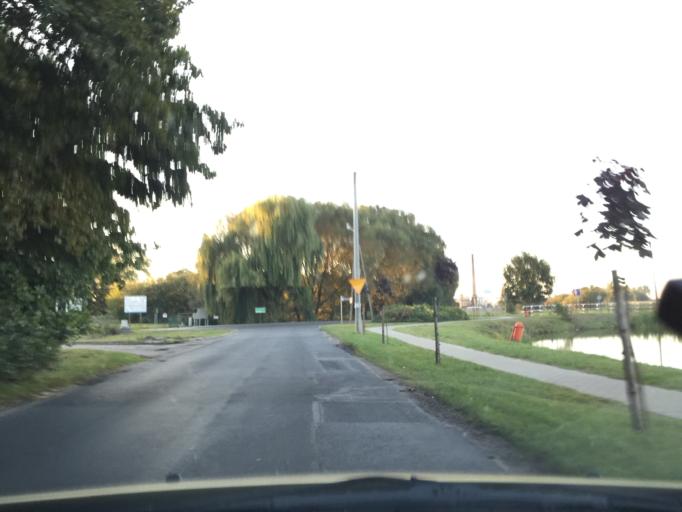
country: PL
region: Greater Poland Voivodeship
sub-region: Powiat pleszewski
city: Dobrzyca
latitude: 51.8666
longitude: 17.6077
